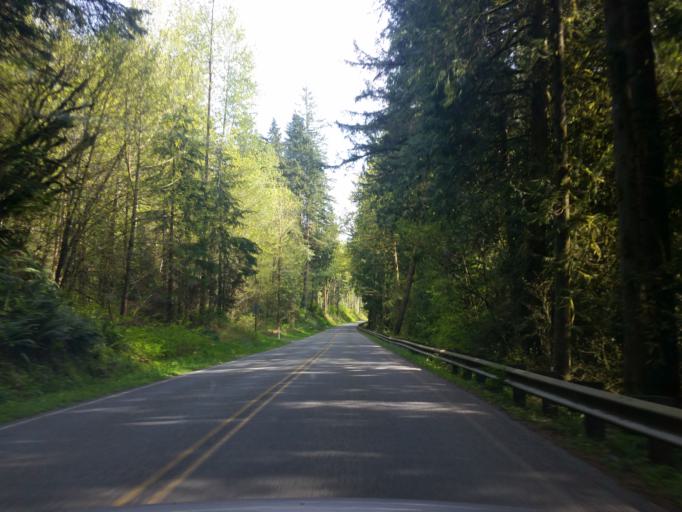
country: US
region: Washington
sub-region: Snohomish County
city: Granite Falls
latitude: 48.0639
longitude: -121.9333
